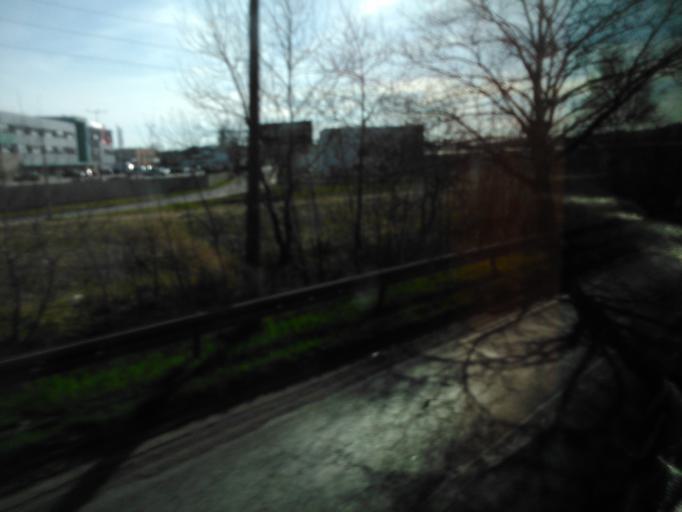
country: PL
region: Kujawsko-Pomorskie
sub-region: Torun
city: Torun
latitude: 52.9908
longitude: 18.6625
